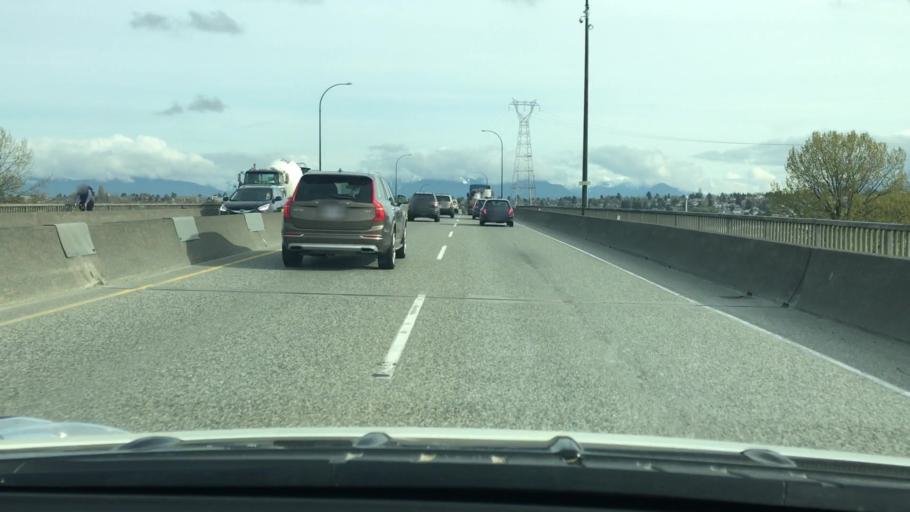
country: CA
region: British Columbia
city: Vancouver
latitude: 49.2001
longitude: -123.0776
